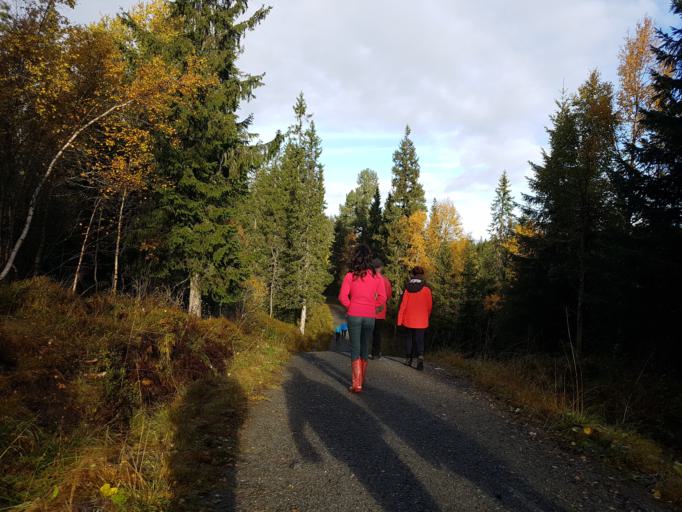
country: NO
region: Sor-Trondelag
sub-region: Trondheim
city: Trondheim
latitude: 63.4204
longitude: 10.2824
